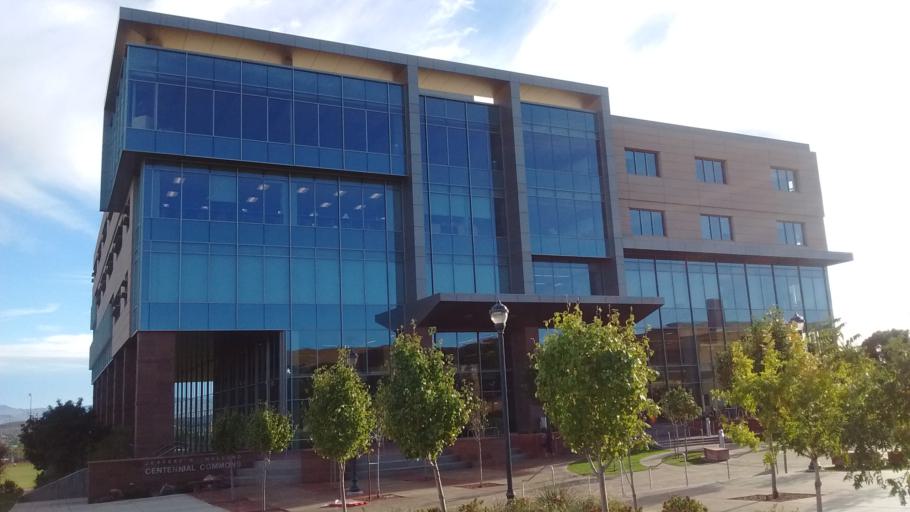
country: US
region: Utah
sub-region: Washington County
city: Saint George
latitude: 37.1034
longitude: -113.5656
